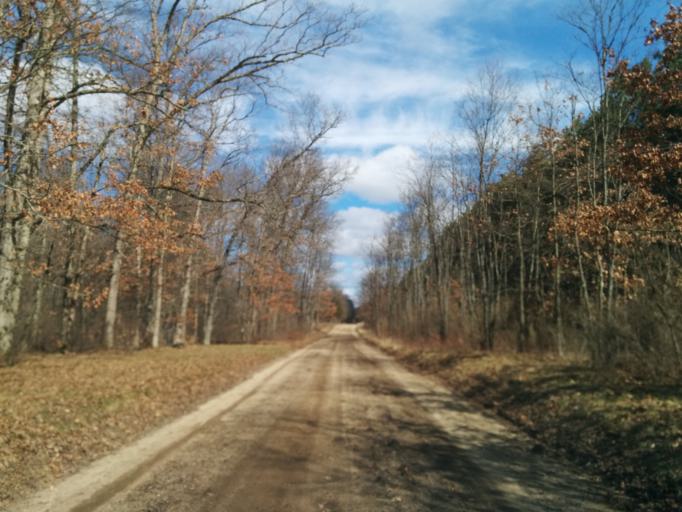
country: US
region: Michigan
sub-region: Newaygo County
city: Newaygo
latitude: 43.4187
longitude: -85.7274
